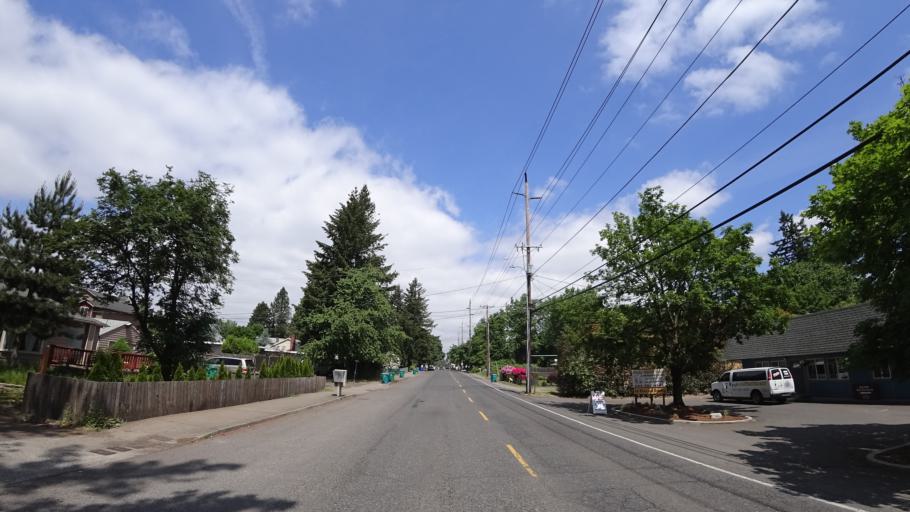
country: US
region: Oregon
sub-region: Multnomah County
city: Gresham
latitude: 45.5023
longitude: -122.4848
